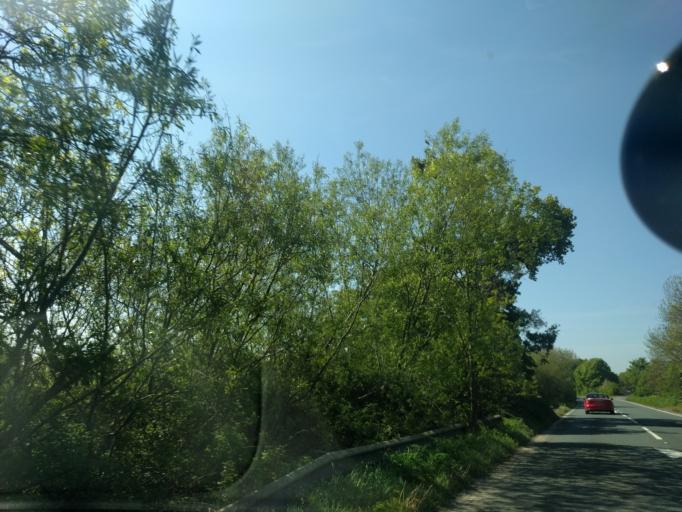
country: GB
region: England
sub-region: Somerset
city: Ilchester
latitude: 51.0310
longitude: -2.6614
